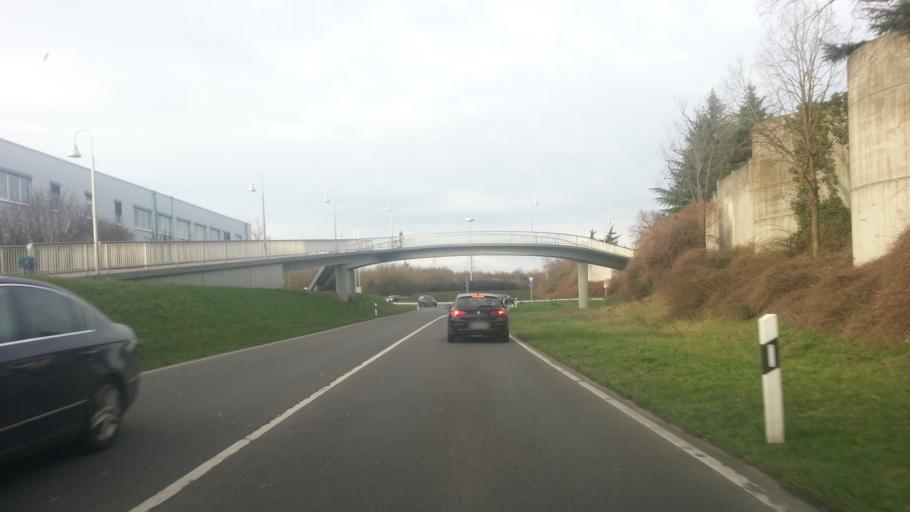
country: DE
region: Baden-Wuerttemberg
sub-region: Karlsruhe Region
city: Walldorf
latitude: 49.3075
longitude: 8.6316
